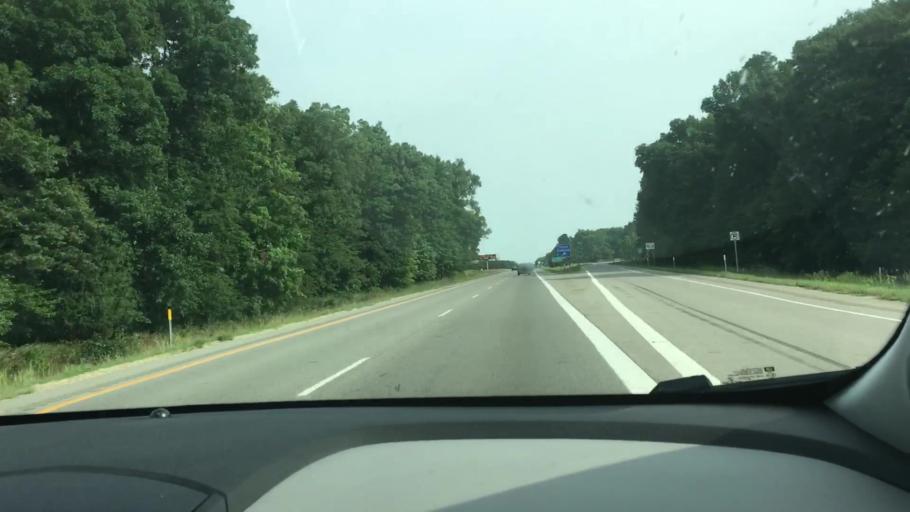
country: US
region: Michigan
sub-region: Kalamazoo County
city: Schoolcraft
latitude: 42.1689
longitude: -85.6446
